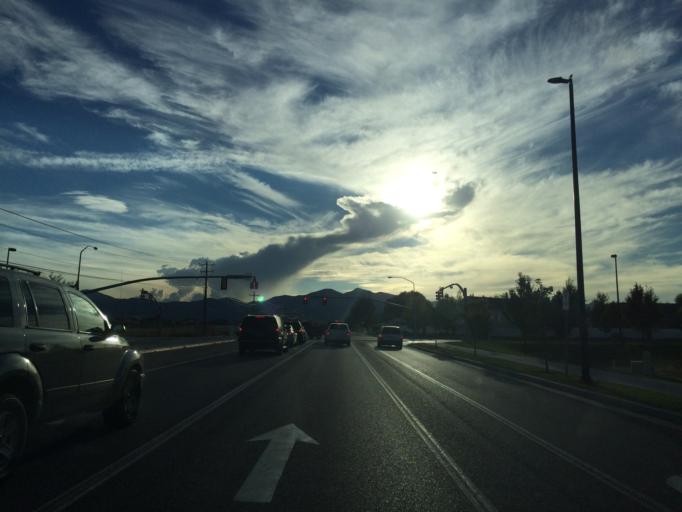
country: US
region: Utah
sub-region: Salt Lake County
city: Oquirrh
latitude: 40.6094
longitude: -112.0045
